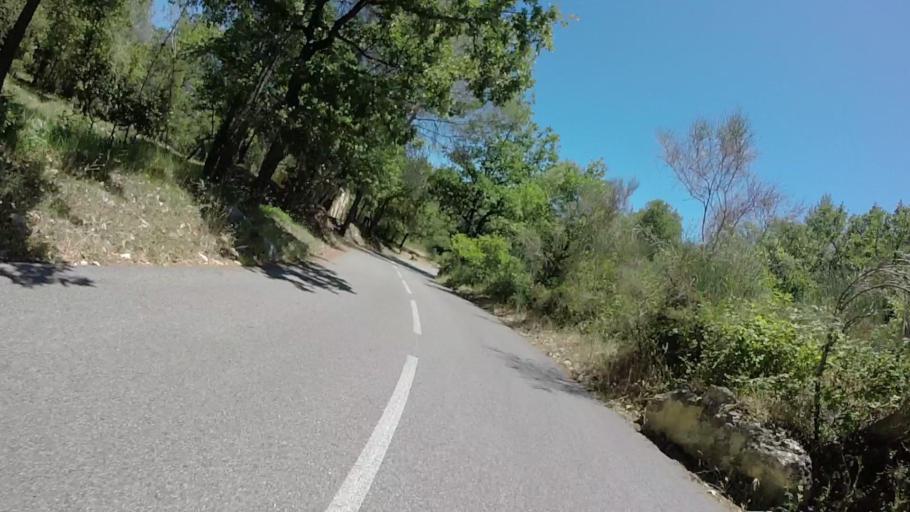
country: FR
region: Provence-Alpes-Cote d'Azur
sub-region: Departement des Alpes-Maritimes
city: Valbonne
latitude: 43.6383
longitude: 7.0453
